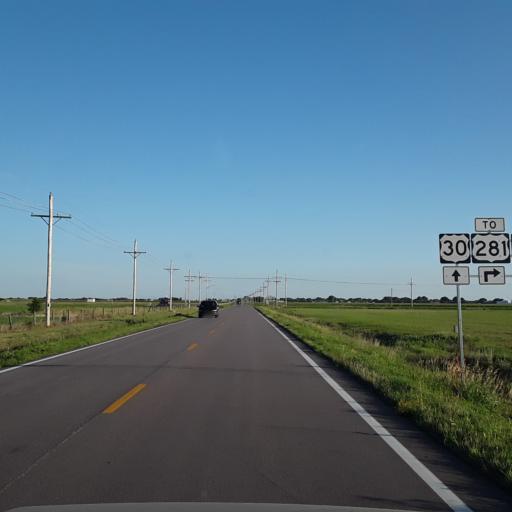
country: US
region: Nebraska
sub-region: Hall County
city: Grand Island
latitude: 40.9620
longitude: -98.3208
